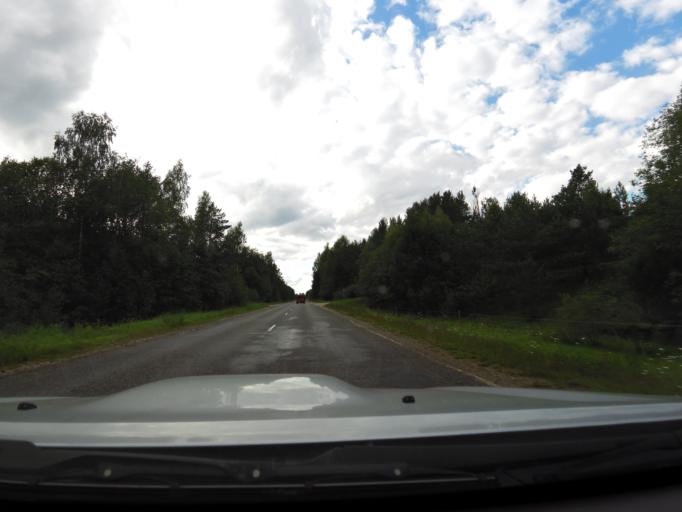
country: LV
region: Akniste
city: Akniste
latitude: 56.0068
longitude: 25.9425
